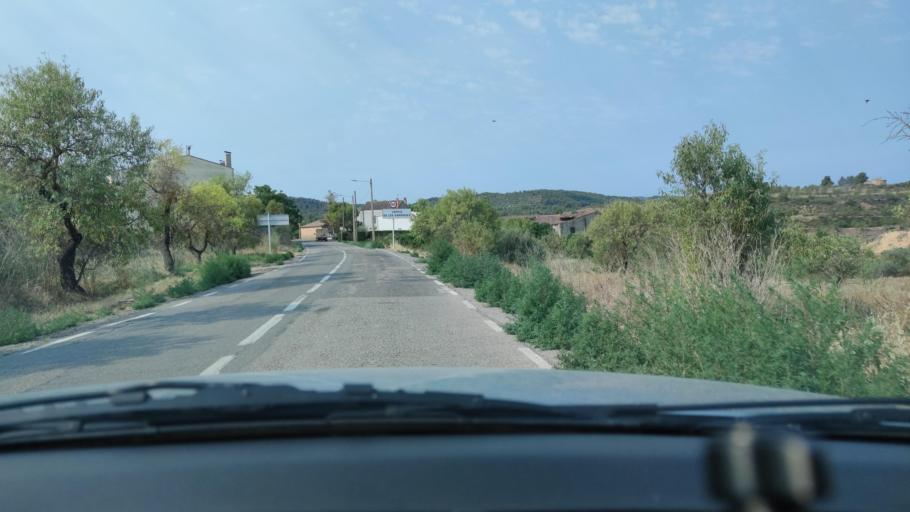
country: ES
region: Catalonia
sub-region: Provincia de Lleida
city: Juncosa
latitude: 41.4288
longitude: 0.8604
